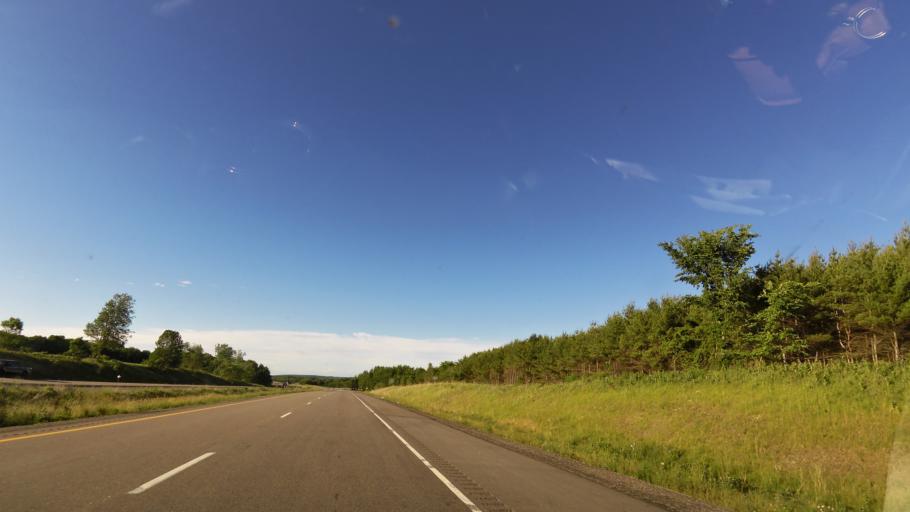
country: CA
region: Ontario
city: Barrie
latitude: 44.6130
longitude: -79.6657
